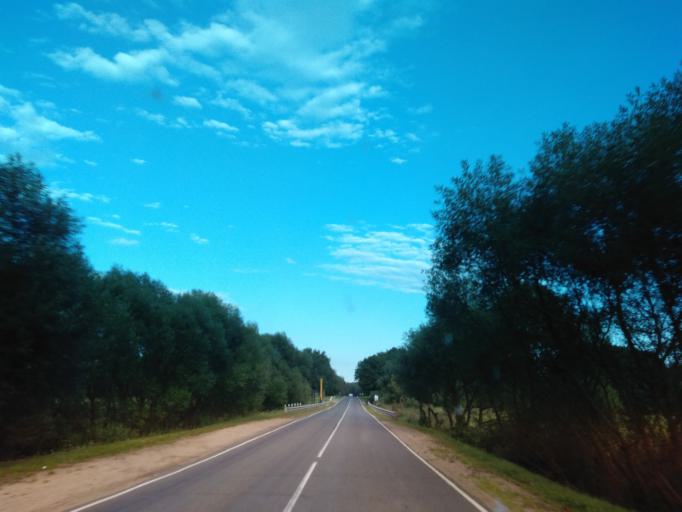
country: BY
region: Minsk
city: Uzda
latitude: 53.4205
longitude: 27.4035
